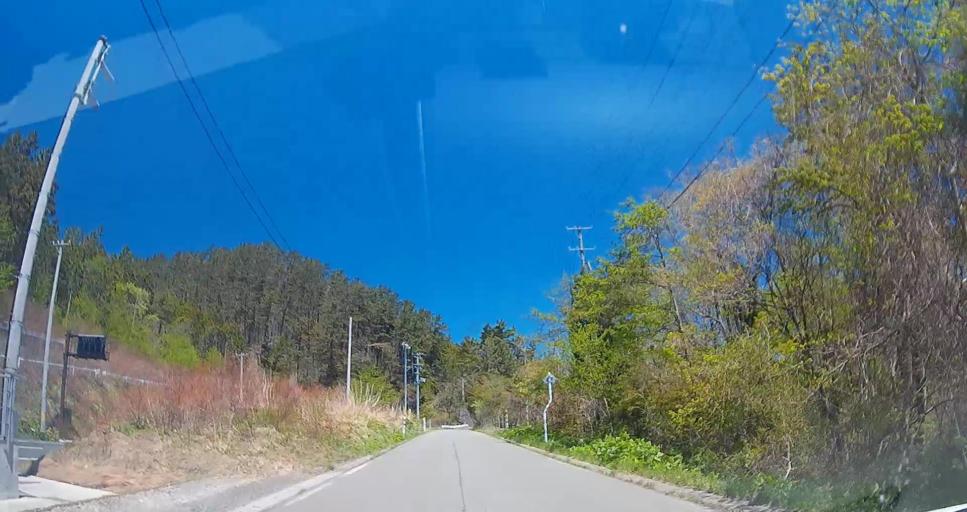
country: JP
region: Aomori
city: Mutsu
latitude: 41.1180
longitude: 141.3913
